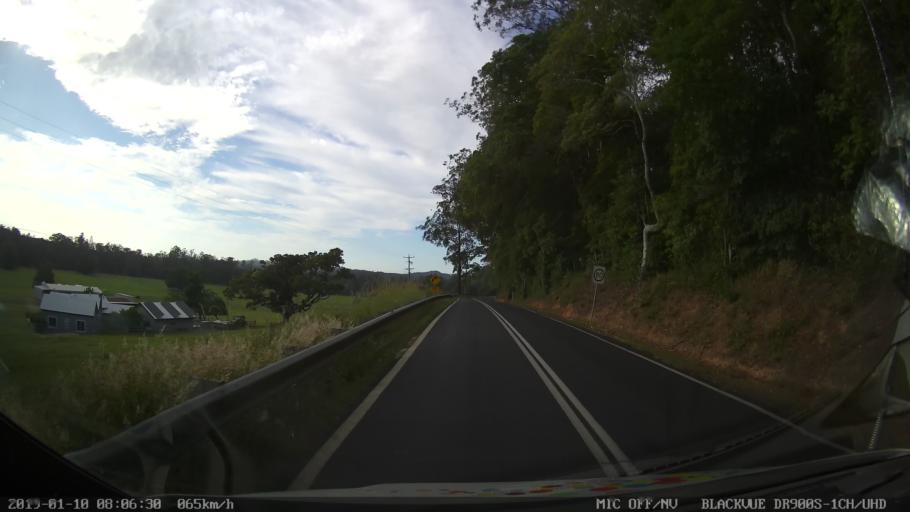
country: AU
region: New South Wales
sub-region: Bellingen
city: Bellingen
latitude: -30.4218
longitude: 152.8506
